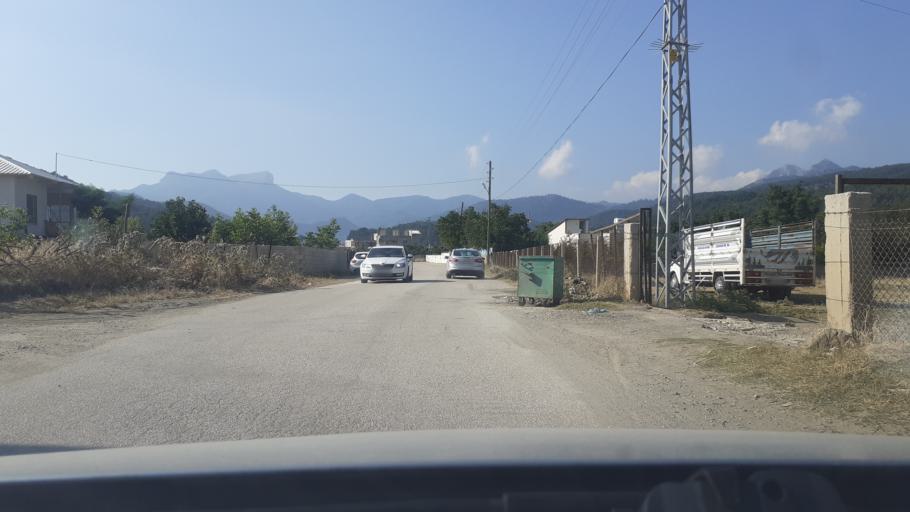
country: TR
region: Hatay
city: Gyuvench
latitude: 36.6208
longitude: 36.3437
